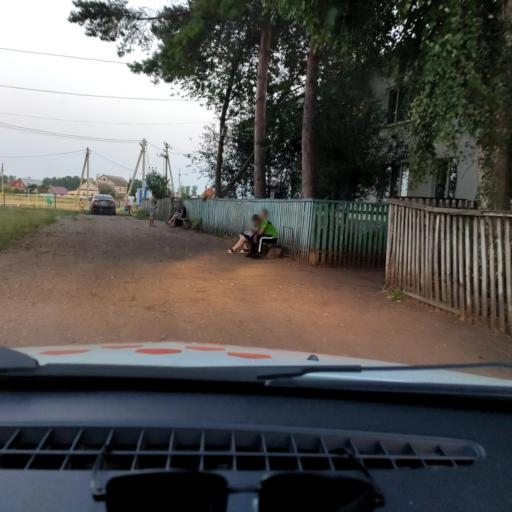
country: RU
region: Bashkortostan
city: Ulukulevo
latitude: 54.3691
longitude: 56.4321
